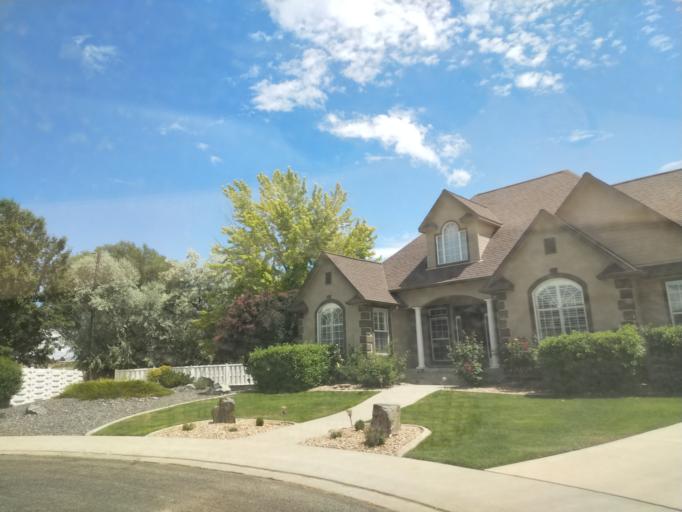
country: US
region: Colorado
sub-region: Mesa County
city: Redlands
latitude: 39.0712
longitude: -108.6463
